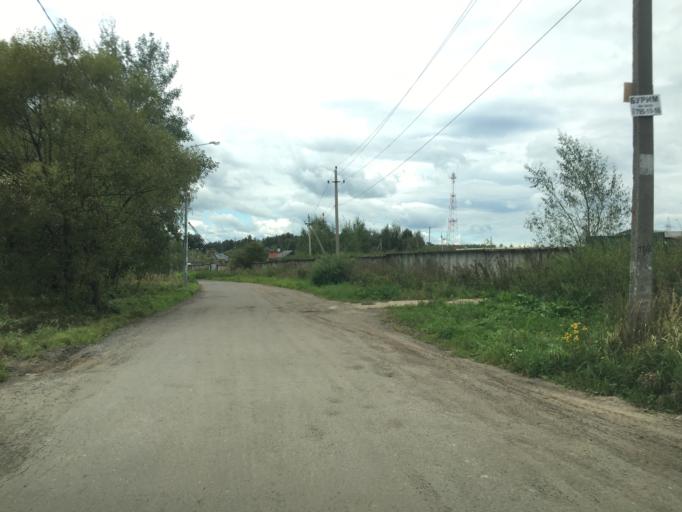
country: RU
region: Moskovskaya
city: Vatutinki
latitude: 55.4785
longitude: 37.4067
